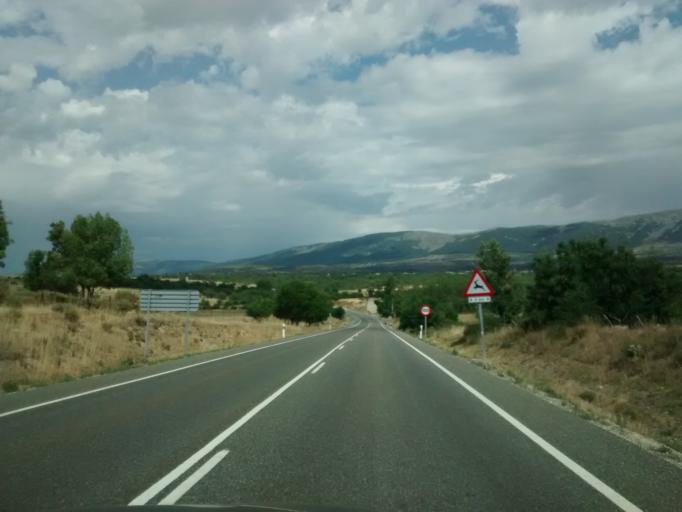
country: ES
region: Castille and Leon
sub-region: Provincia de Segovia
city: Navafria
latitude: 41.0640
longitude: -3.8308
